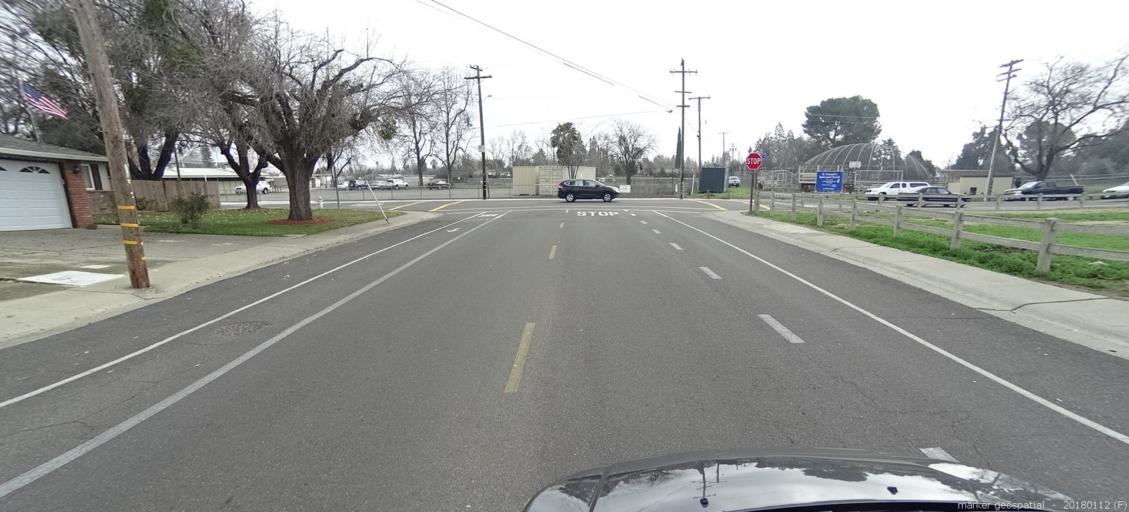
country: US
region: California
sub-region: Sacramento County
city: Rancho Cordova
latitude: 38.6045
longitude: -121.2889
